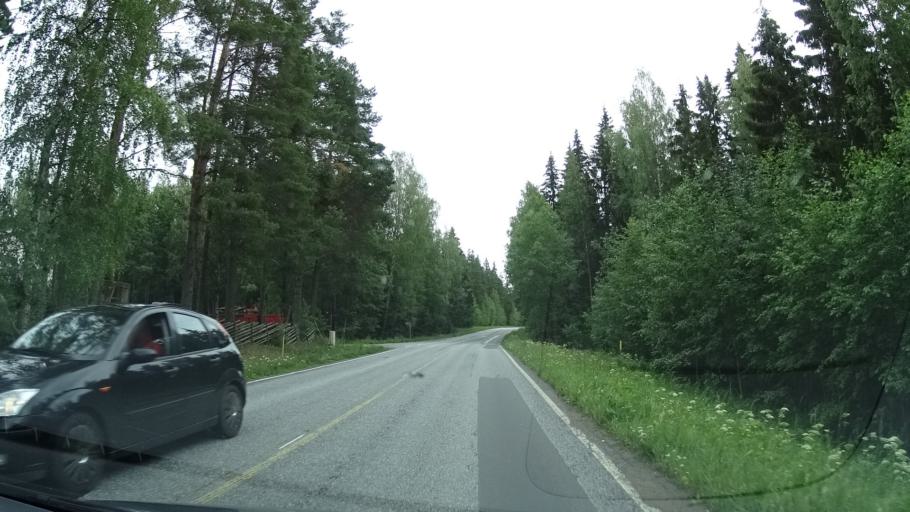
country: FI
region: Pirkanmaa
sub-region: Etelae-Pirkanmaa
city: Urjala
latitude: 61.0871
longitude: 23.5172
